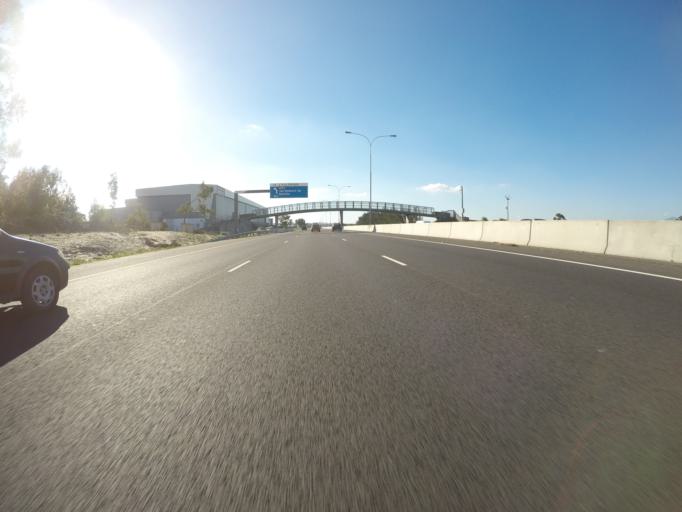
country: ZA
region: Western Cape
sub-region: City of Cape Town
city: Kraaifontein
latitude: -33.9282
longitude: 18.6627
